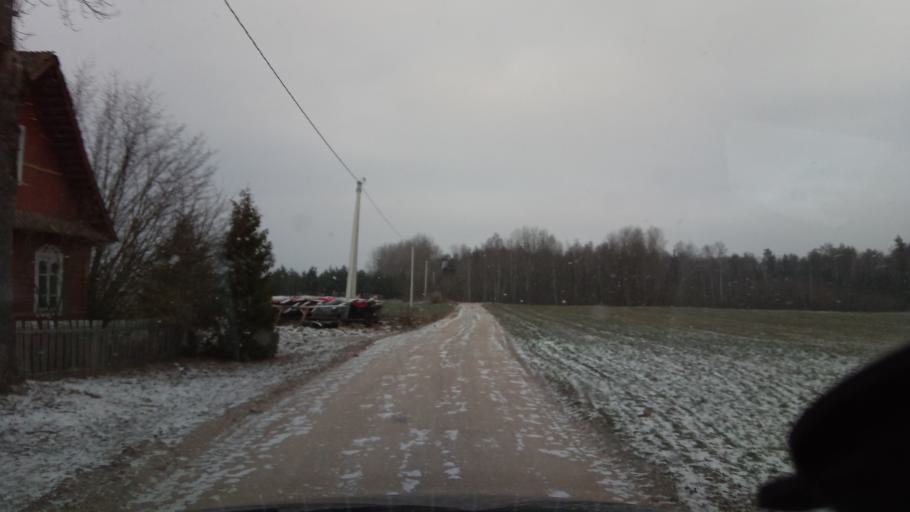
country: LT
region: Alytaus apskritis
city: Varena
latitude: 54.1292
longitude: 24.7040
